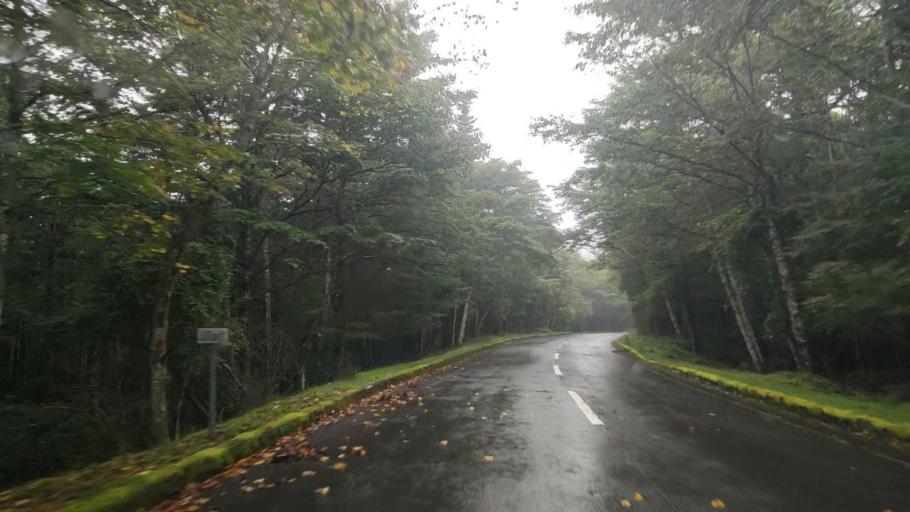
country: JP
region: Shizuoka
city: Fujinomiya
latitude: 35.3164
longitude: 138.7312
